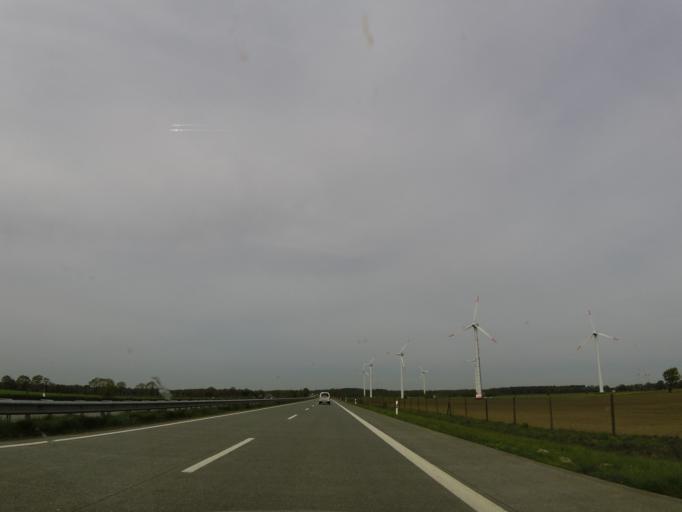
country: DE
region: Schleswig-Holstein
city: Bokelrehm
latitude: 54.0504
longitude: 9.3929
